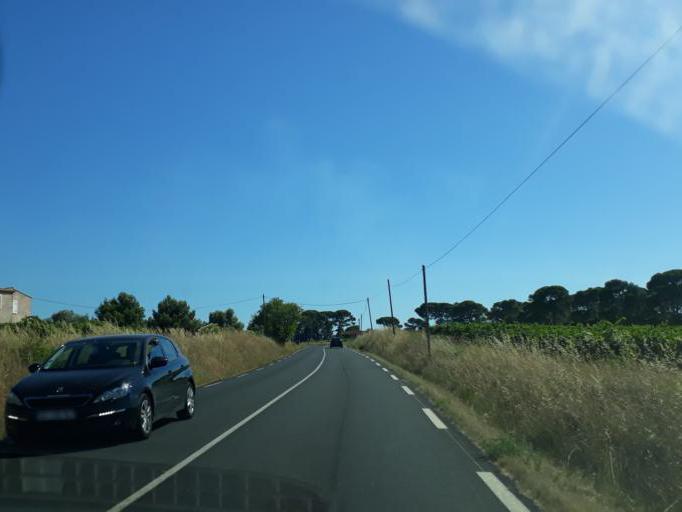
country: FR
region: Languedoc-Roussillon
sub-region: Departement de l'Herault
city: Agde
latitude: 43.3445
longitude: 3.4872
